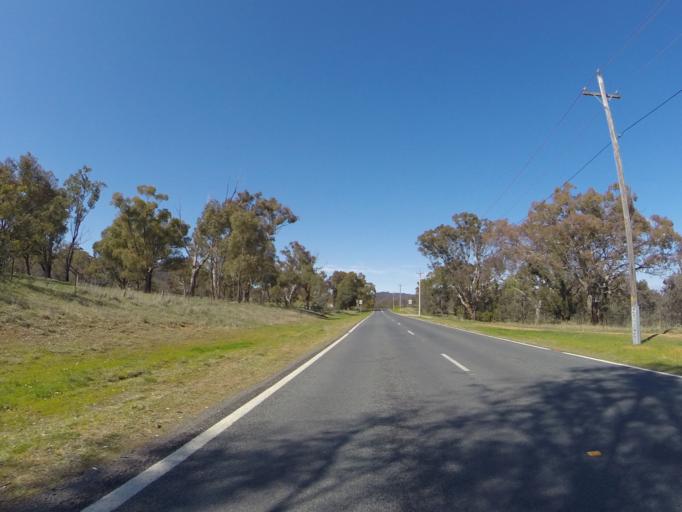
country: AU
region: Australian Capital Territory
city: Canberra
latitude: -35.2350
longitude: 149.1663
